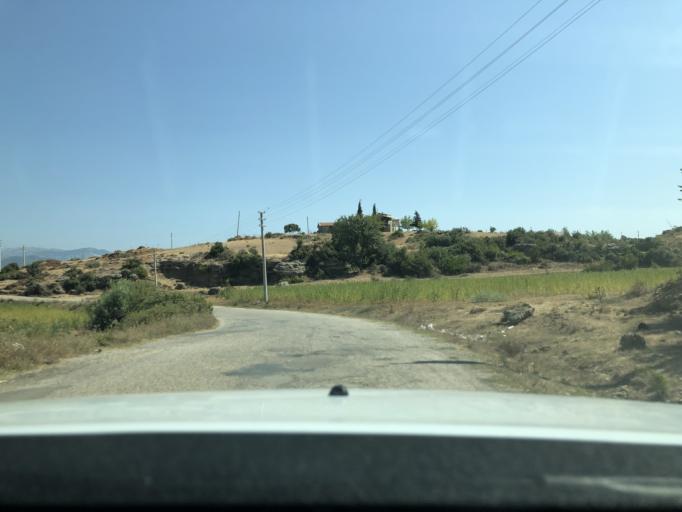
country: TR
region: Antalya
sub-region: Manavgat
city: Manavgat
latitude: 36.8029
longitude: 31.4705
